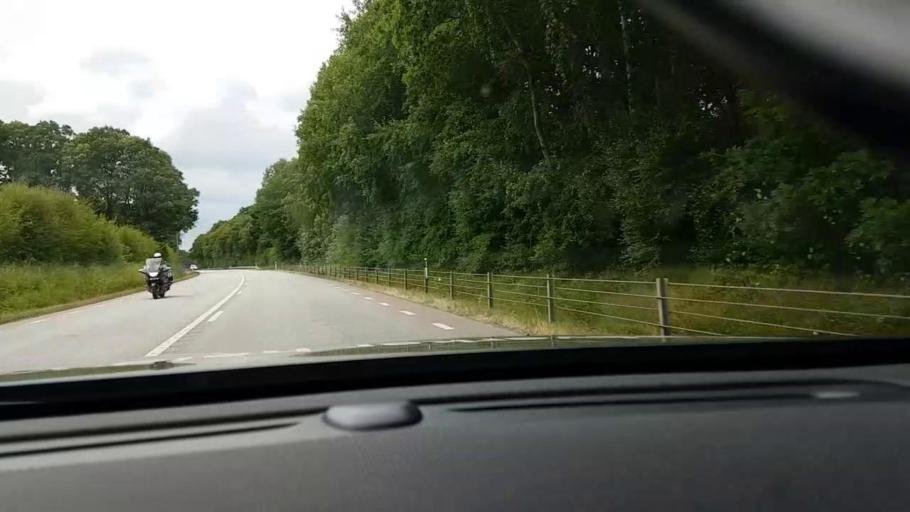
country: SE
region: Skane
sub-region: Horby Kommun
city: Hoerby
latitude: 55.8684
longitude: 13.6376
